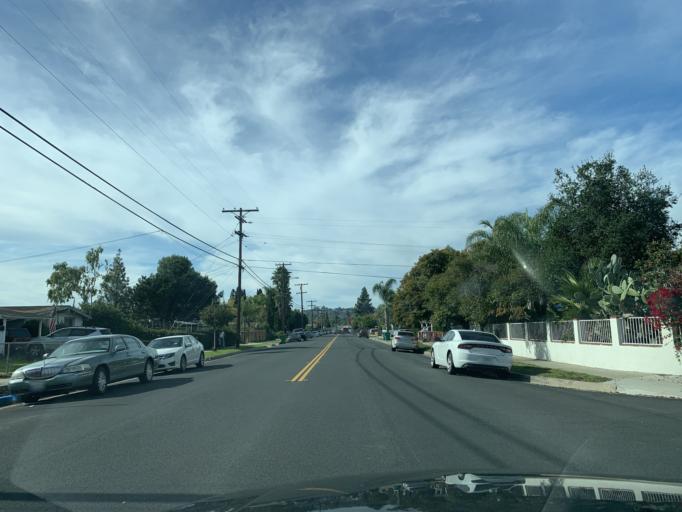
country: US
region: California
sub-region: San Diego County
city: El Cajon
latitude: 32.8006
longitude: -116.9531
